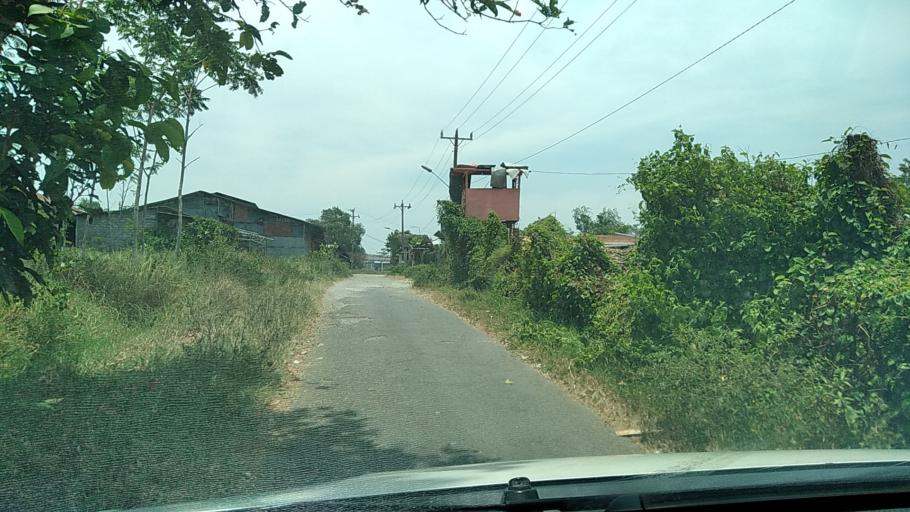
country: ID
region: Central Java
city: Ungaran
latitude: -7.0956
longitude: 110.3097
